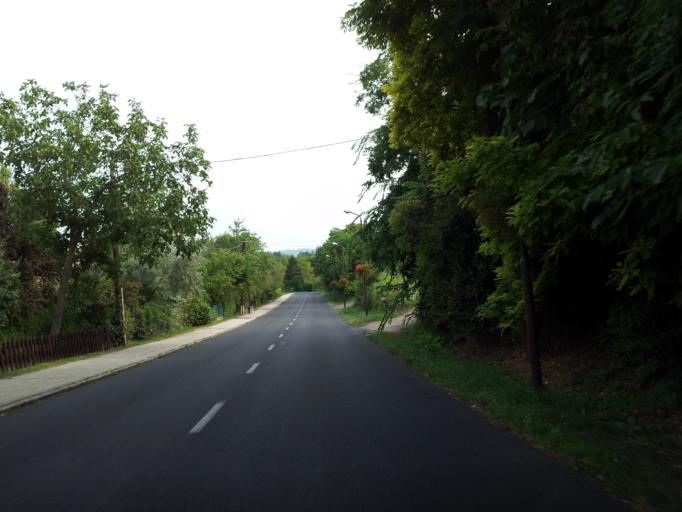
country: HU
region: Veszprem
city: Tihany
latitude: 46.8967
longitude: 17.8893
